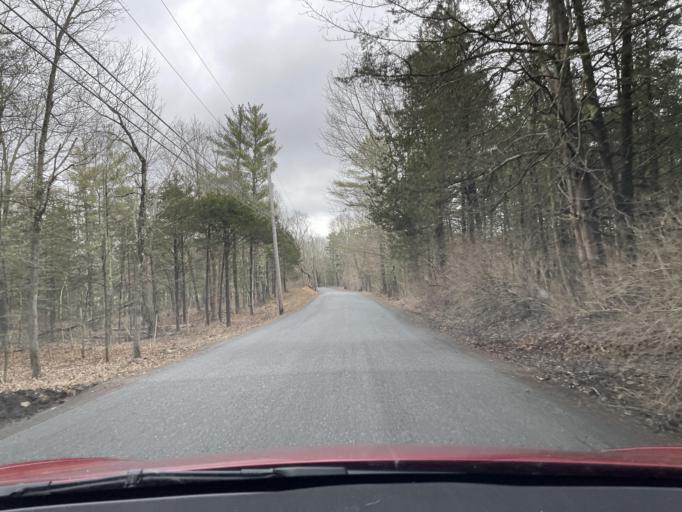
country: US
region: New York
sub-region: Ulster County
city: Manorville
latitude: 42.0867
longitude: -74.0358
